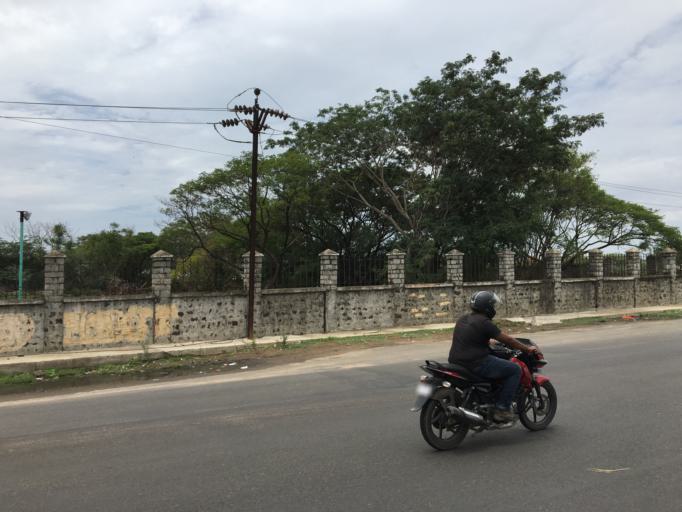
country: IN
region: Tamil Nadu
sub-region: Kancheepuram
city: Madipakkam
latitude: 12.9458
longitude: 80.2090
